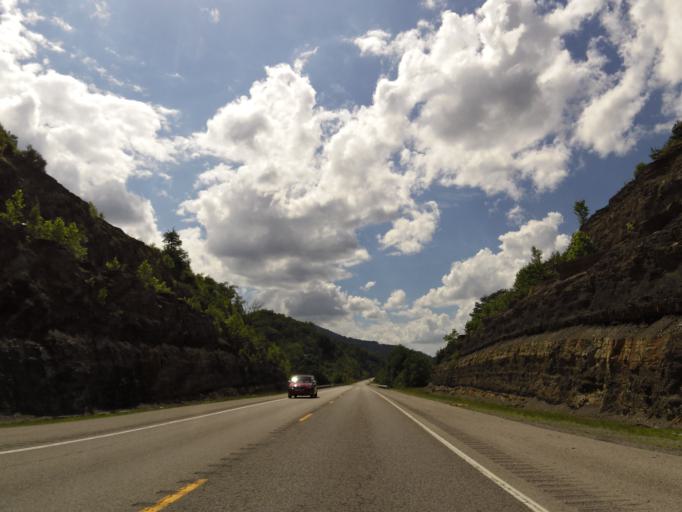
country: US
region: Kentucky
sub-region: Harlan County
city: Harlan
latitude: 36.7816
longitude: -83.2335
